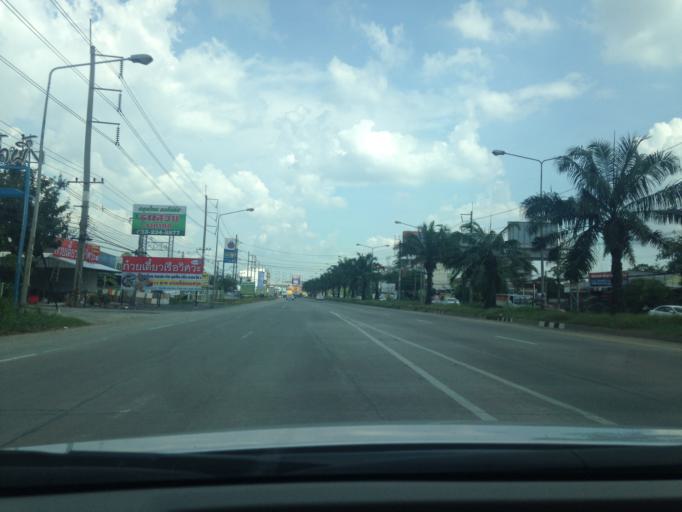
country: TH
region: Pathum Thani
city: Pathum Thani
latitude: 14.0301
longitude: 100.5284
